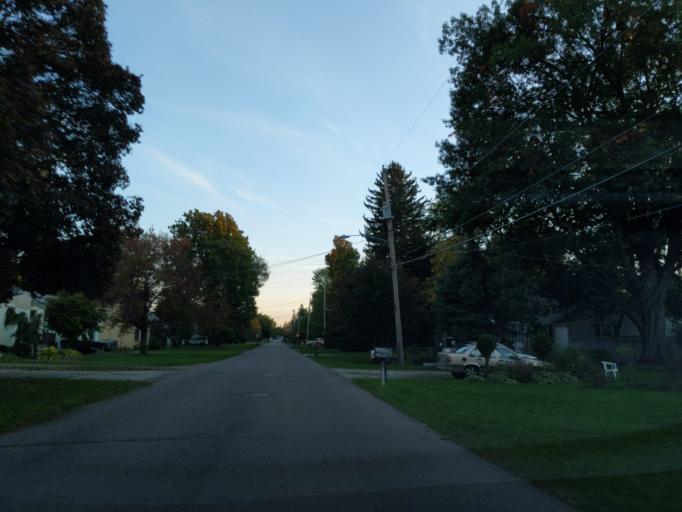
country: US
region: Michigan
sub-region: Ingham County
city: Edgemont Park
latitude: 42.7311
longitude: -84.5980
